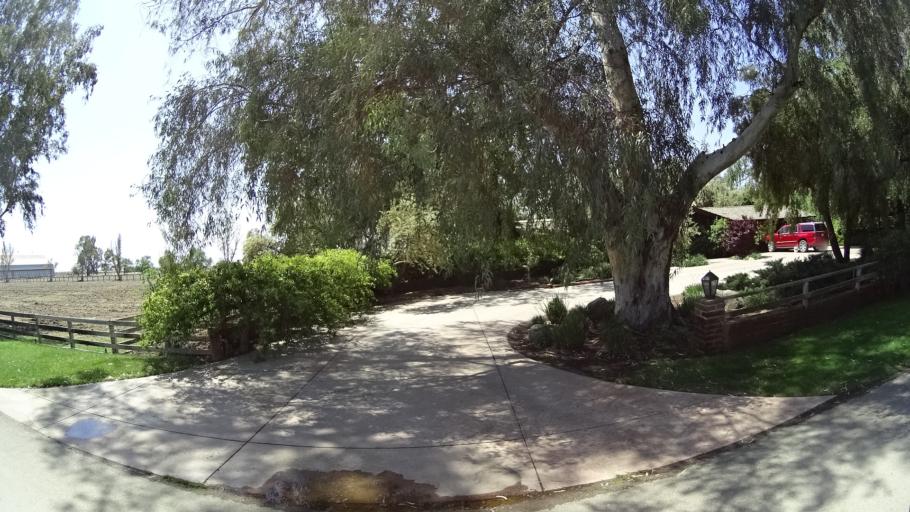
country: US
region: California
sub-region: Kings County
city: Stratford
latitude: 36.1235
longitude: -119.8878
